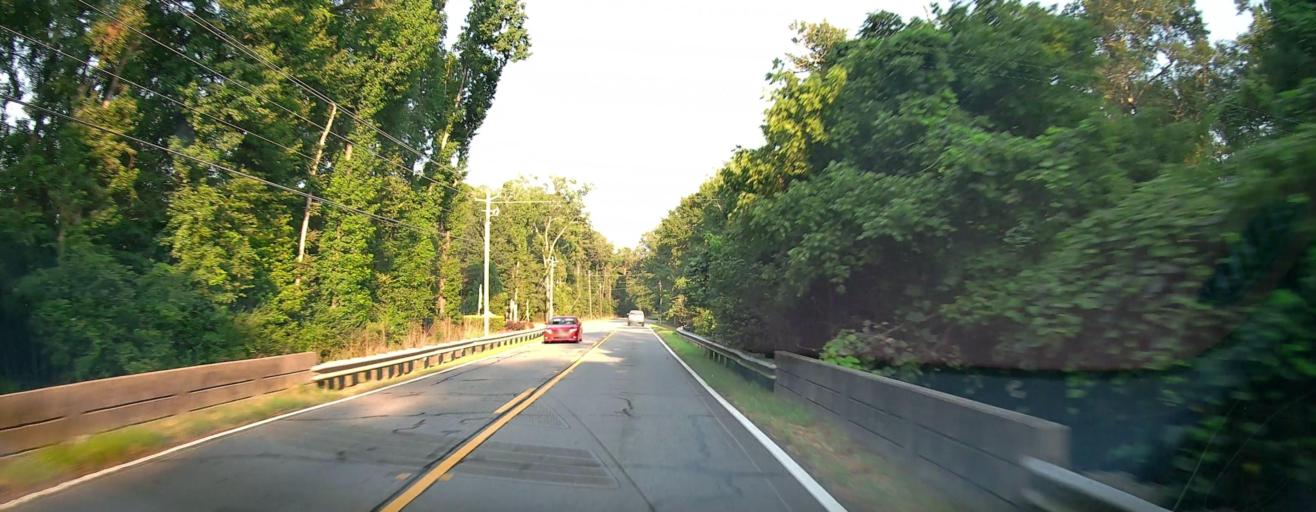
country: US
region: Georgia
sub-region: Bibb County
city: Macon
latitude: 32.8850
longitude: -83.7339
